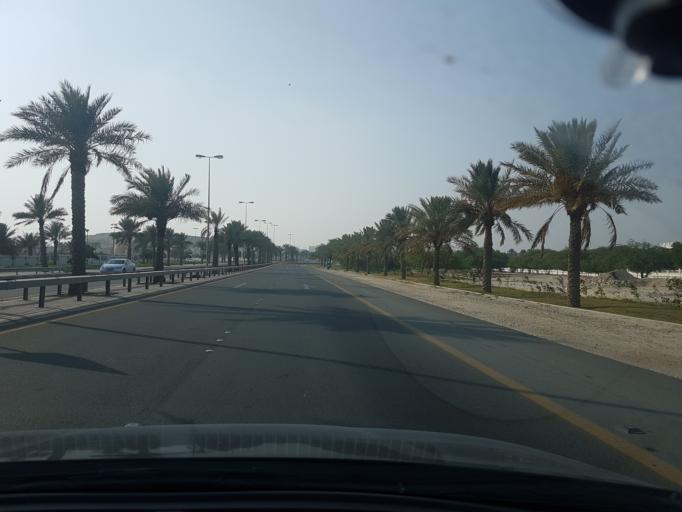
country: BH
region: Northern
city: Ar Rifa'
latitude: 26.1063
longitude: 50.5405
